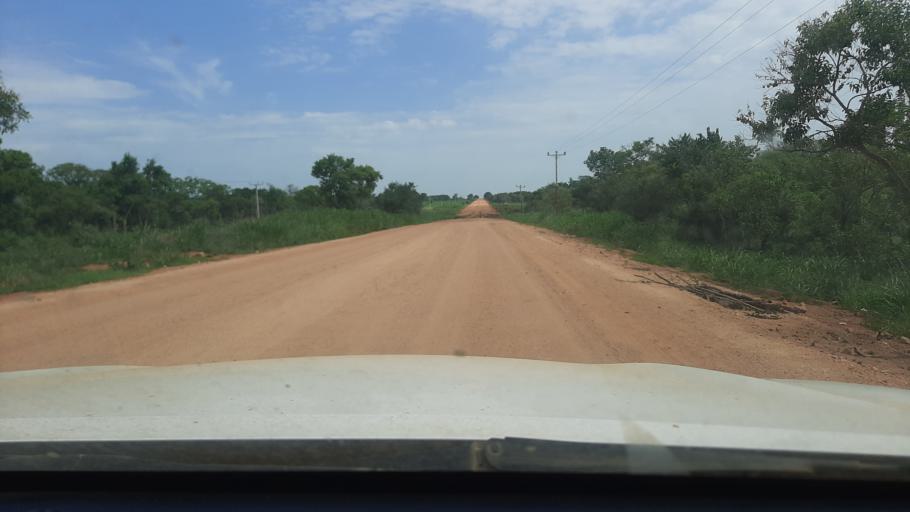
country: ET
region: Gambela
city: Gambela
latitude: 8.0207
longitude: 34.5734
